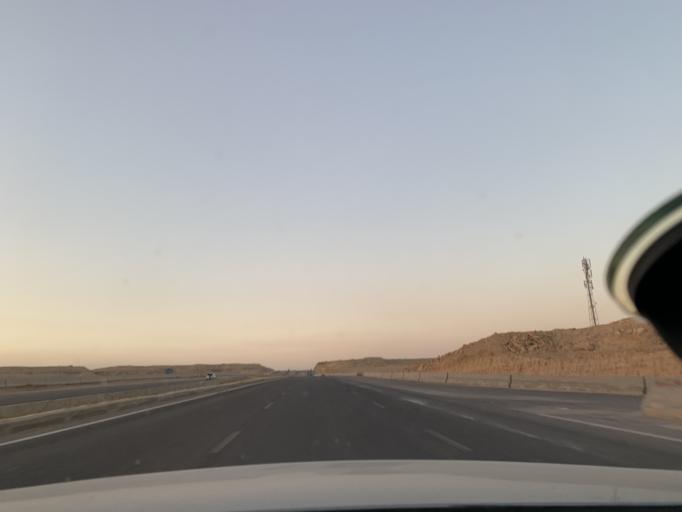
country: EG
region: Muhafazat al Qahirah
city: Halwan
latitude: 29.9400
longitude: 31.5310
